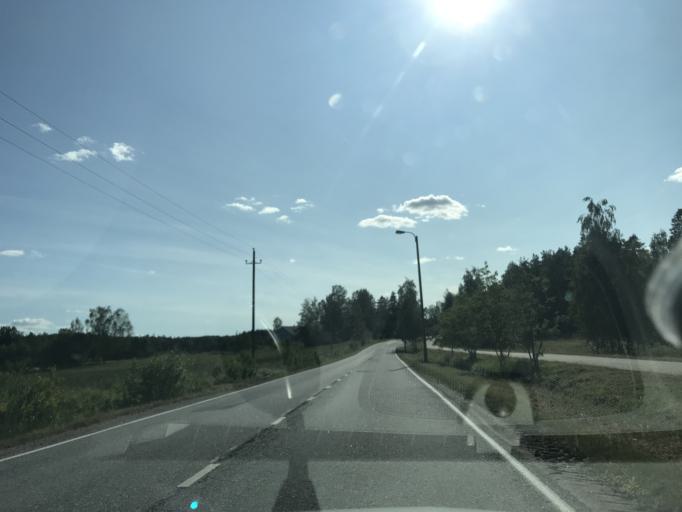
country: FI
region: Uusimaa
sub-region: Helsinki
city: Nurmijaervi
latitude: 60.3820
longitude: 24.6723
